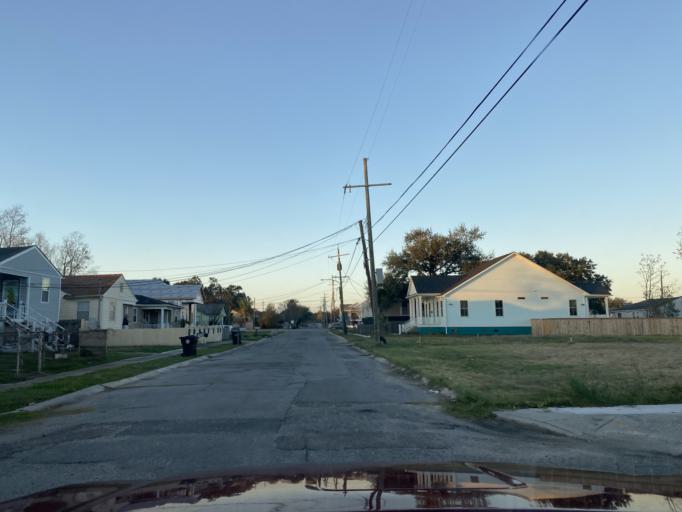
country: US
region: Louisiana
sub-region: Orleans Parish
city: New Orleans
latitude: 30.0212
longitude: -90.0552
